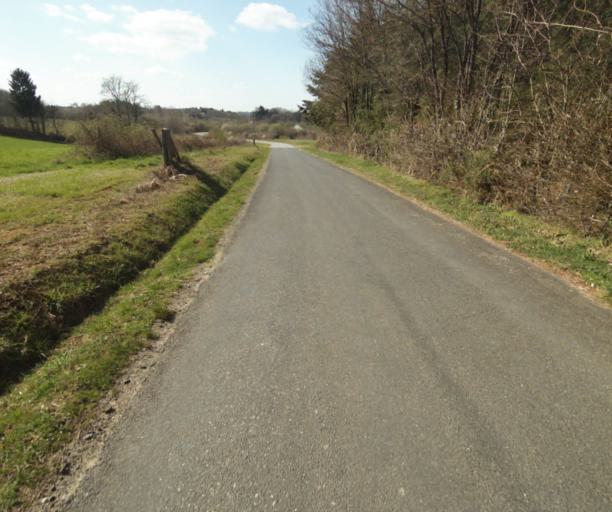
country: FR
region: Limousin
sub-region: Departement de la Correze
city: Saint-Mexant
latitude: 45.3029
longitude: 1.6598
